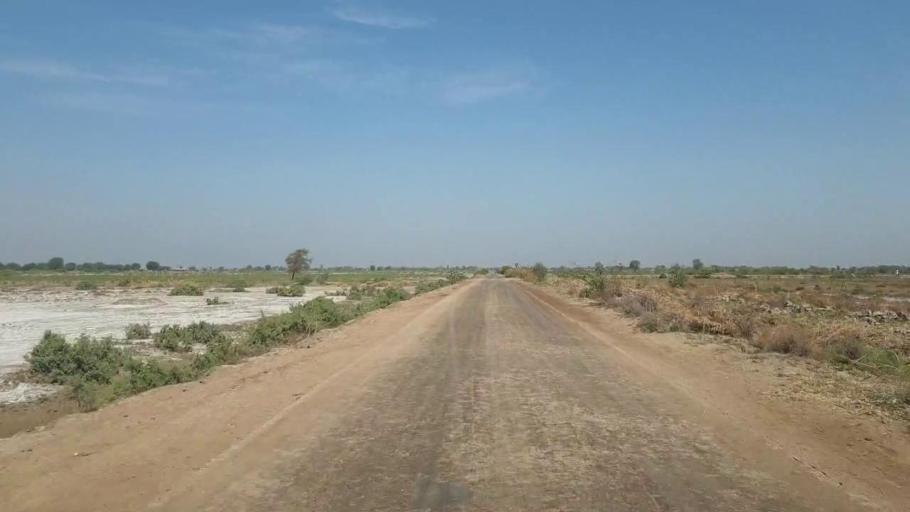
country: PK
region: Sindh
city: Samaro
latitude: 25.3717
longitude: 69.2585
